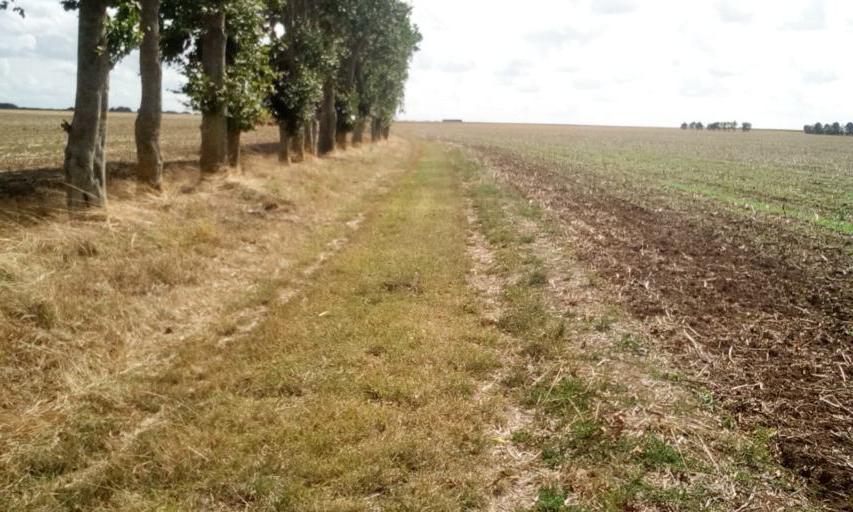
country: FR
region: Lower Normandy
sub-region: Departement du Calvados
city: Saint-Sylvain
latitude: 49.0874
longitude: -0.1965
